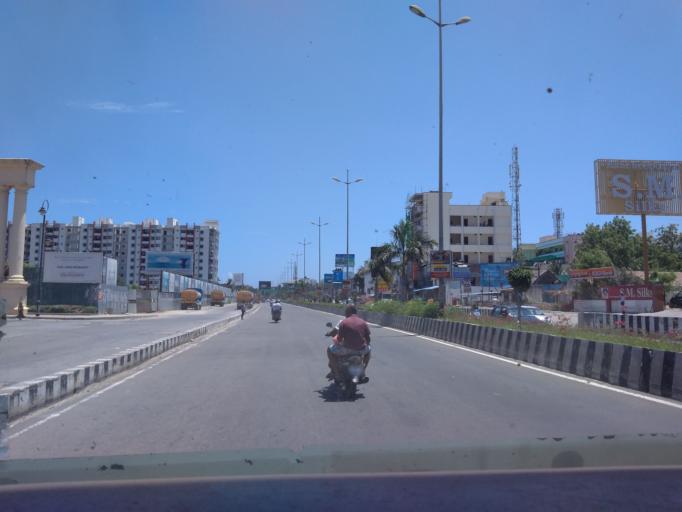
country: IN
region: Tamil Nadu
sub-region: Kancheepuram
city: Injambakkam
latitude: 12.8353
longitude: 80.2286
